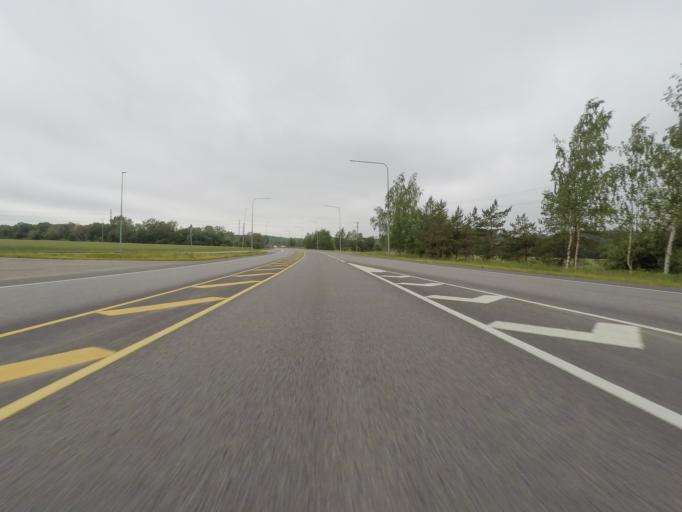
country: FI
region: Varsinais-Suomi
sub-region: Turku
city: Raisio
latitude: 60.4618
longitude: 22.1944
